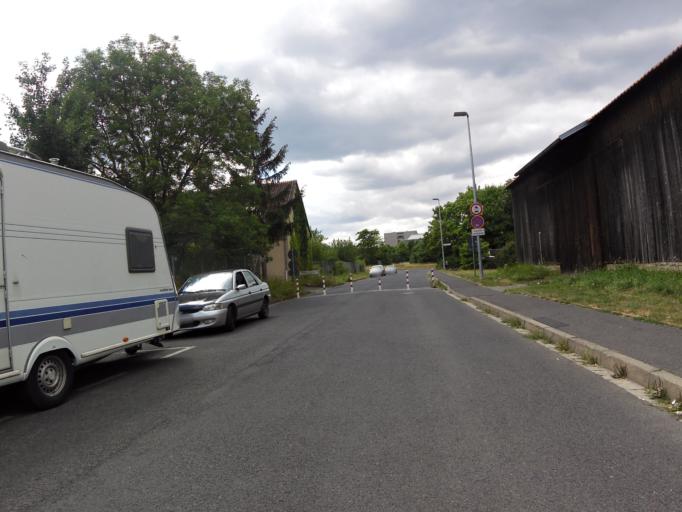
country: DE
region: Bavaria
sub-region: Regierungsbezirk Unterfranken
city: Gerbrunn
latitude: 49.7800
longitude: 9.9759
